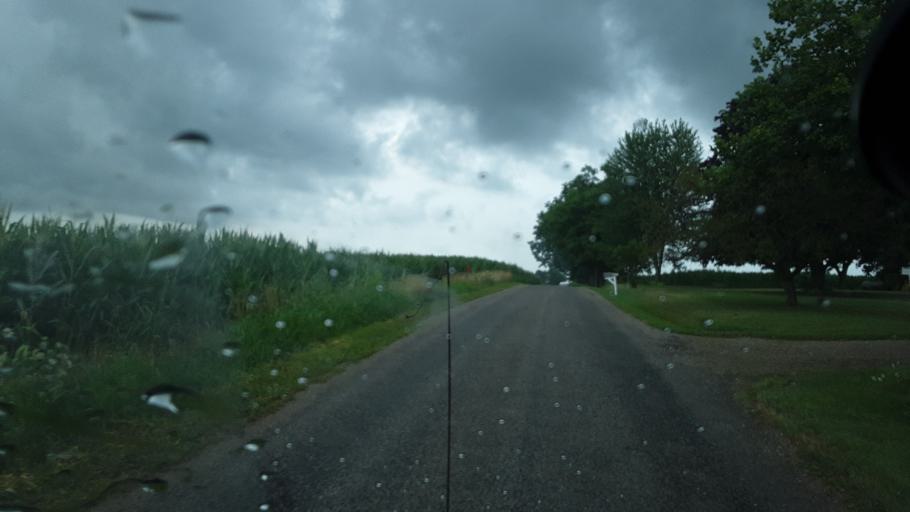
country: US
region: Indiana
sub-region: Steuben County
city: Hamilton
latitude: 41.5374
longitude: -84.8299
